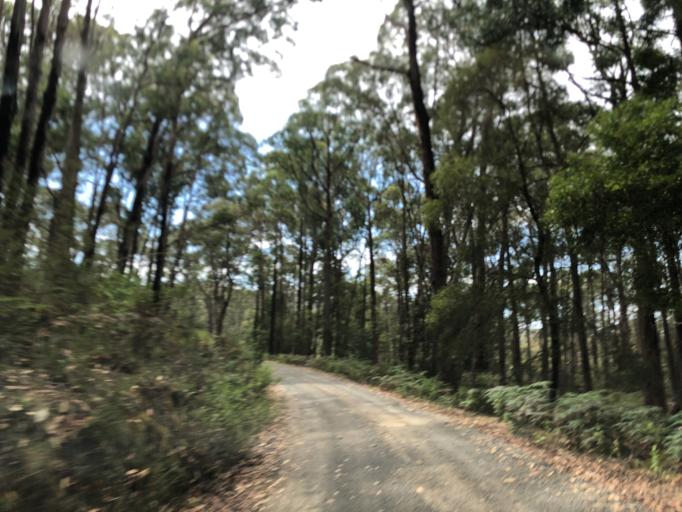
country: AU
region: Victoria
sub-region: Moorabool
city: Bacchus Marsh
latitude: -37.4720
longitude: 144.2836
